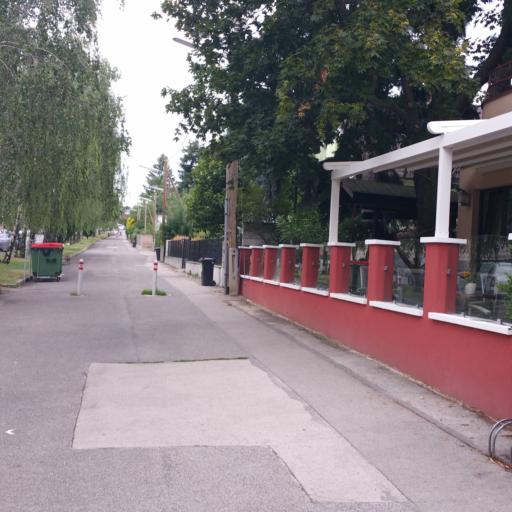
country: AT
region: Vienna
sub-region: Wien Stadt
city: Vienna
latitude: 48.2049
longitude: 16.3022
